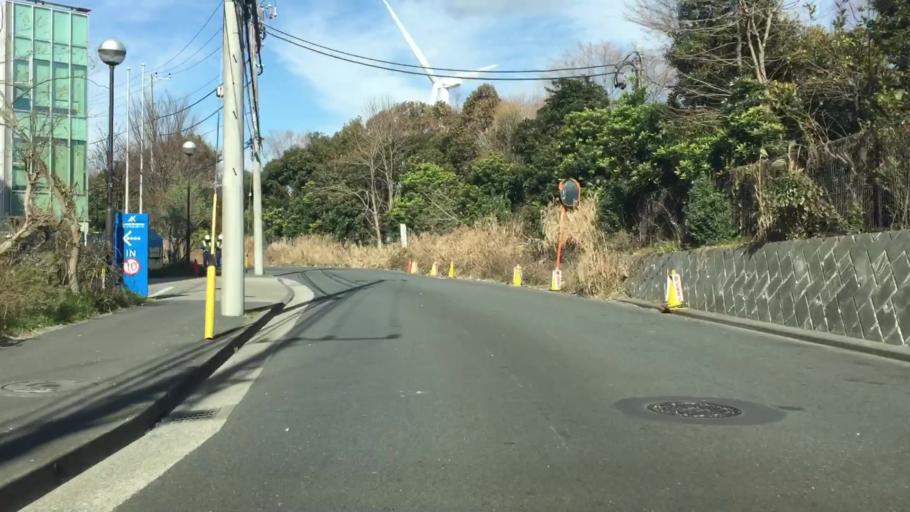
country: JP
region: Tokyo
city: Urayasu
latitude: 35.6193
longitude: 139.8335
